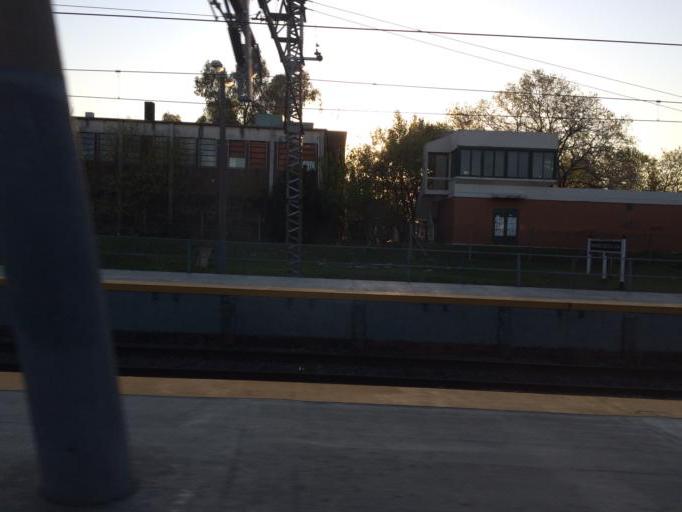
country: AR
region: Buenos Aires
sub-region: Partido de Lanus
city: Lanus
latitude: -34.7281
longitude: -58.3937
